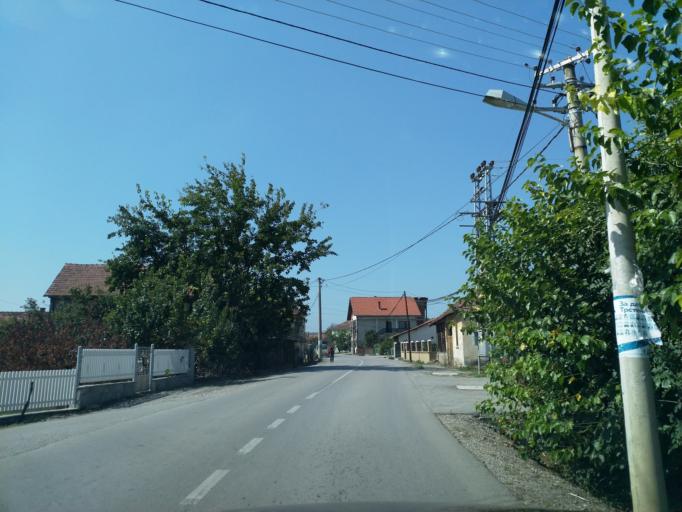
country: RS
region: Central Serbia
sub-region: Rasinski Okrug
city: Trstenik
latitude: 43.6258
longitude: 21.1337
